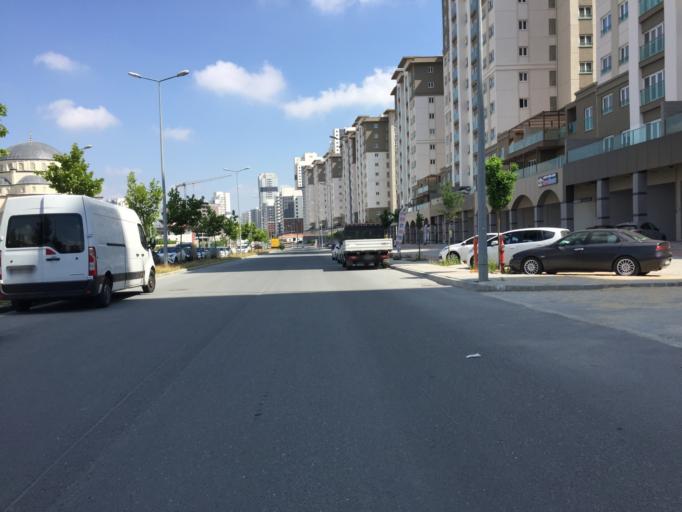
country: TR
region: Istanbul
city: Esenyurt
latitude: 41.0851
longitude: 28.6552
